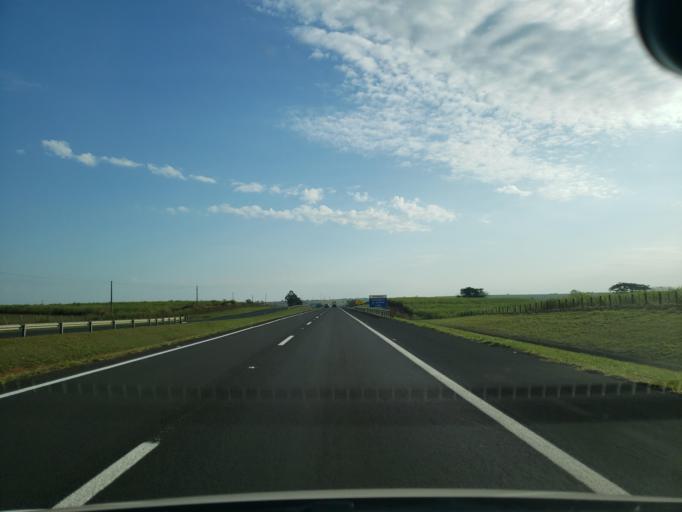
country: BR
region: Sao Paulo
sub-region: Valparaiso
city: Valparaiso
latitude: -21.2081
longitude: -50.8191
